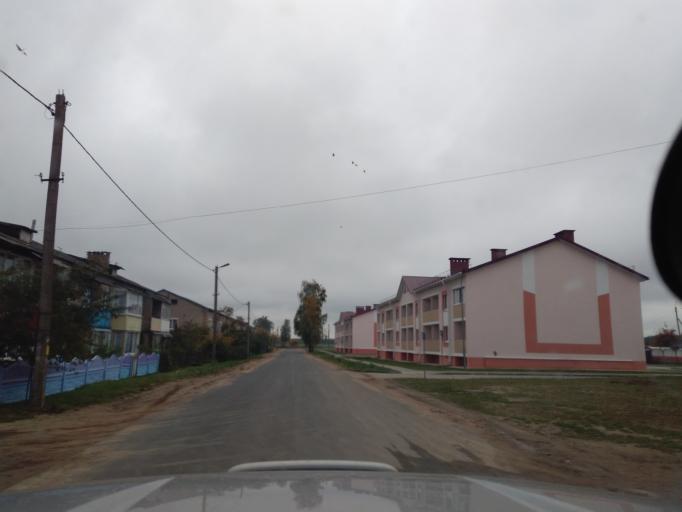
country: BY
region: Minsk
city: Kapyl'
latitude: 53.1399
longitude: 27.0910
